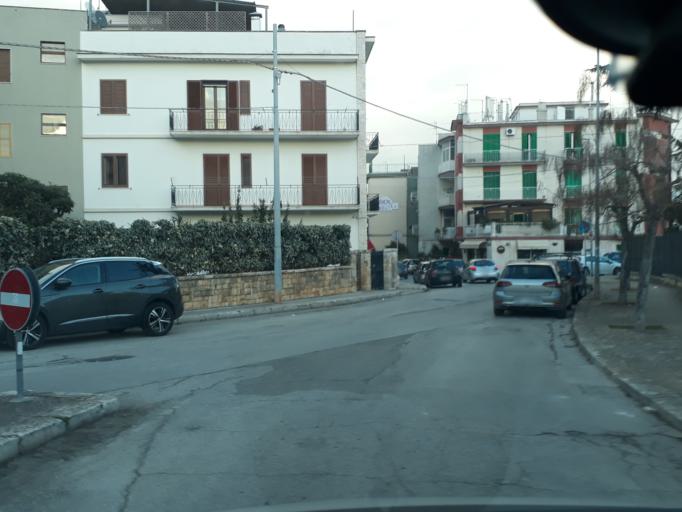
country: IT
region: Apulia
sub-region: Provincia di Brindisi
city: Fasano
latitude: 40.8357
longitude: 17.3533
